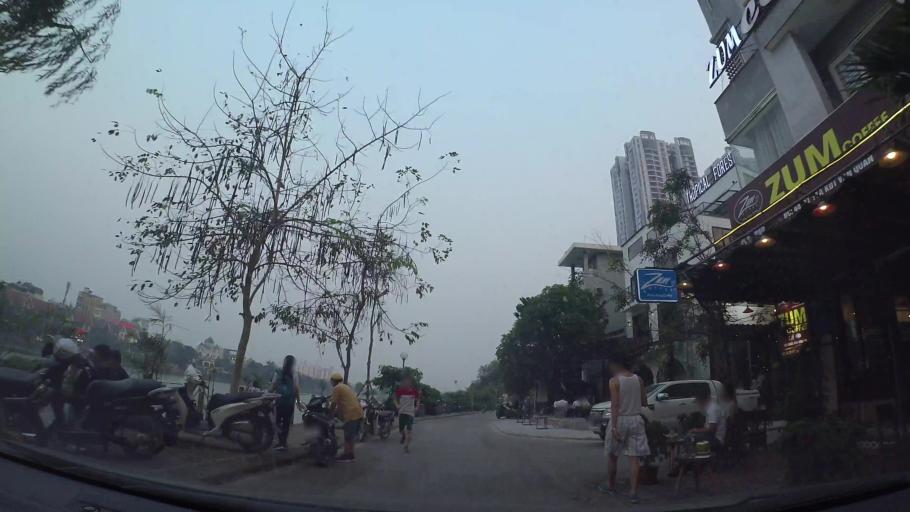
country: VN
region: Ha Noi
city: Ha Dong
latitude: 20.9786
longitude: 105.7897
